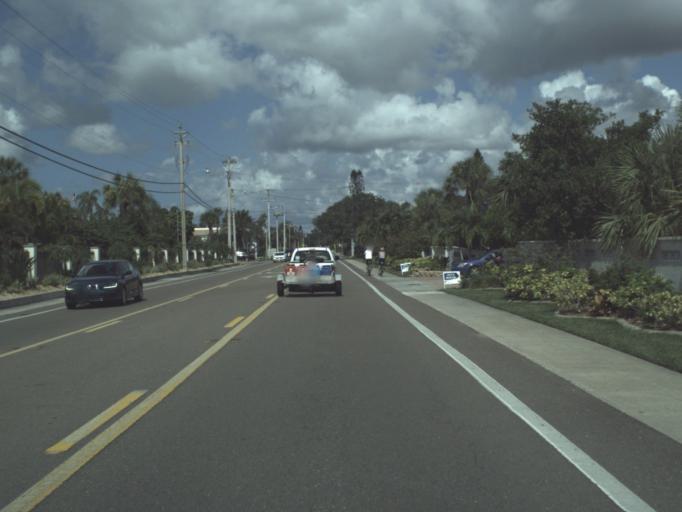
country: US
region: Florida
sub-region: Sarasota County
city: Gulf Gate Estates
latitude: 27.2573
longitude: -82.5376
